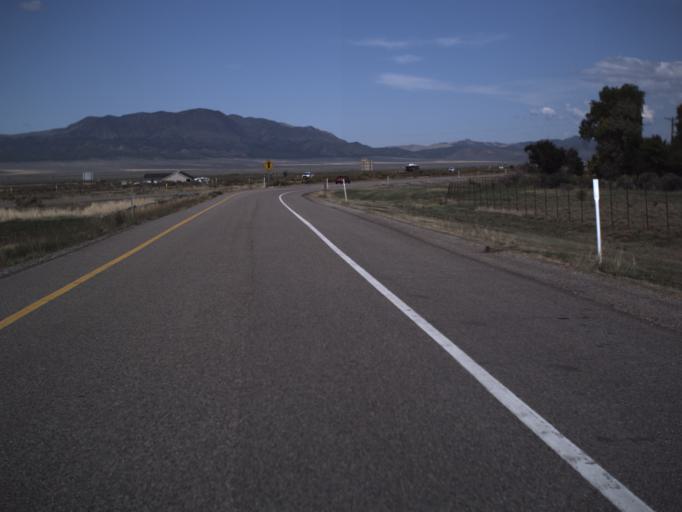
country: US
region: Utah
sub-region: Iron County
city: Parowan
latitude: 37.9093
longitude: -112.7757
